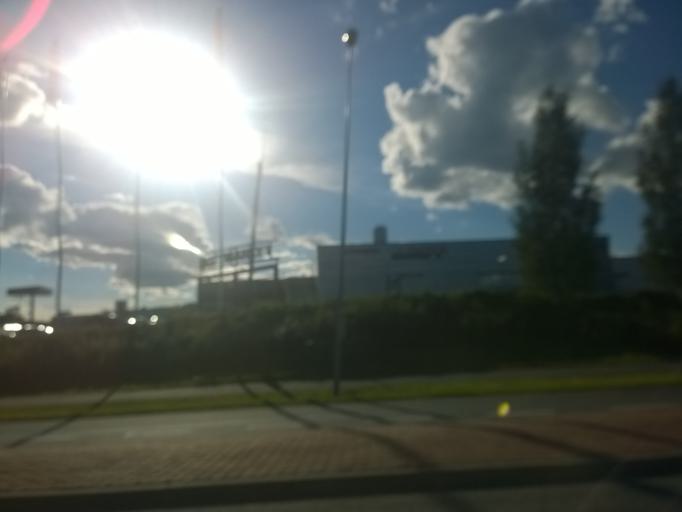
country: FI
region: Pirkanmaa
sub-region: Tampere
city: Tampere
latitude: 61.4658
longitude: 23.7254
